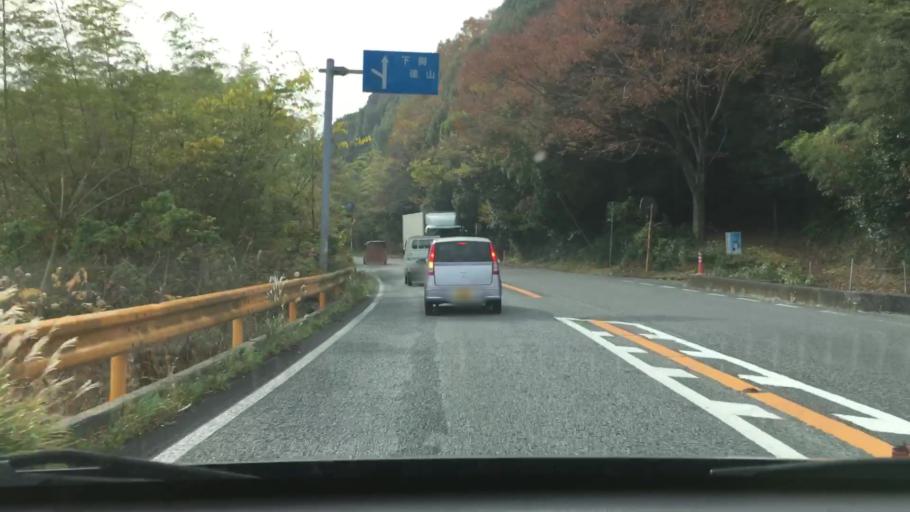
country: JP
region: Yamaguchi
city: Iwakuni
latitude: 34.1059
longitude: 132.1008
